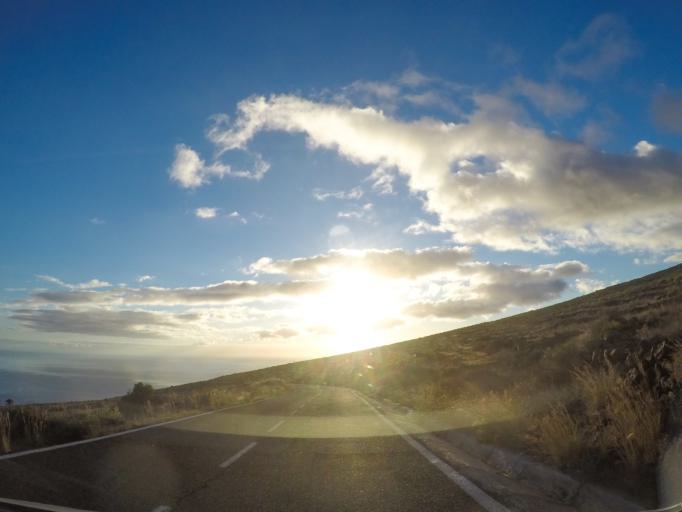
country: ES
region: Canary Islands
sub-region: Provincia de Santa Cruz de Tenerife
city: Alajero
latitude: 28.0443
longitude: -17.2285
